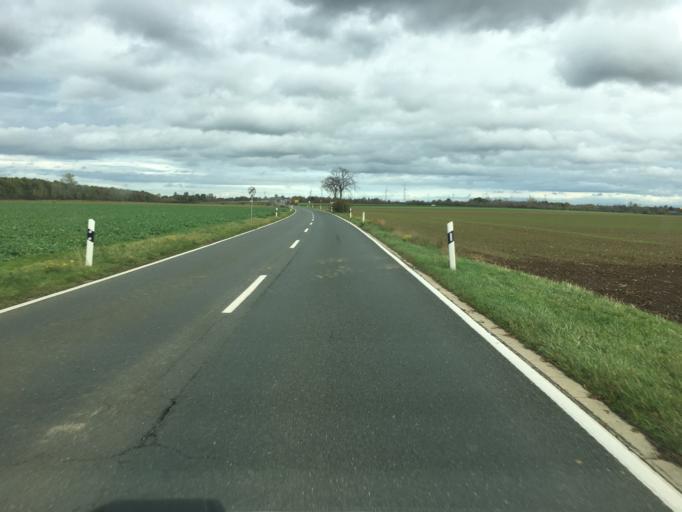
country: DE
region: North Rhine-Westphalia
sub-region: Regierungsbezirk Koln
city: Euskirchen
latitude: 50.6728
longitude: 6.7264
